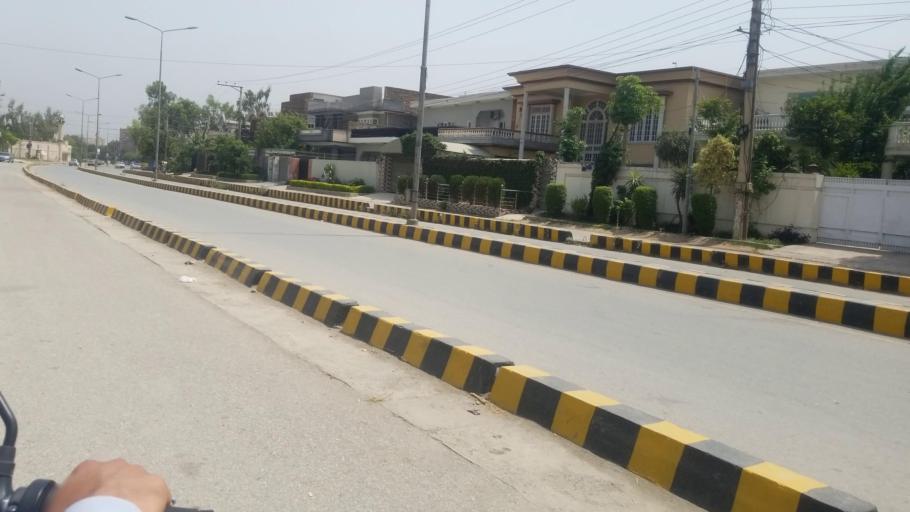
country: PK
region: Khyber Pakhtunkhwa
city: Peshawar
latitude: 33.9944
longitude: 71.4443
